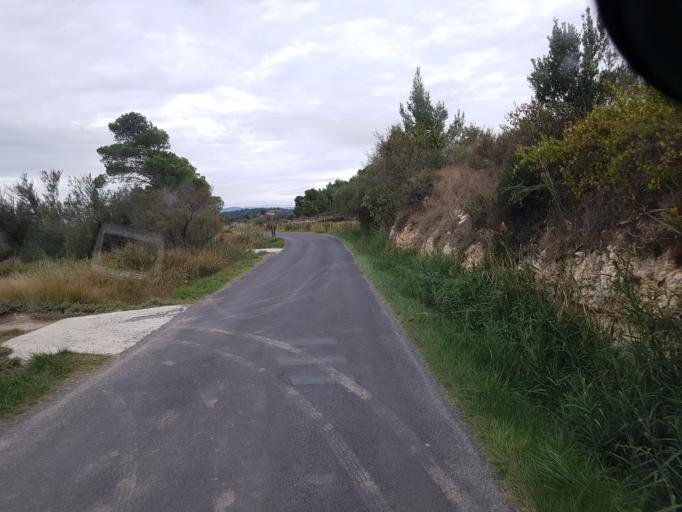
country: FR
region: Languedoc-Roussillon
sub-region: Departement de l'Aude
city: Peyriac-de-Mer
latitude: 43.1200
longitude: 2.9899
